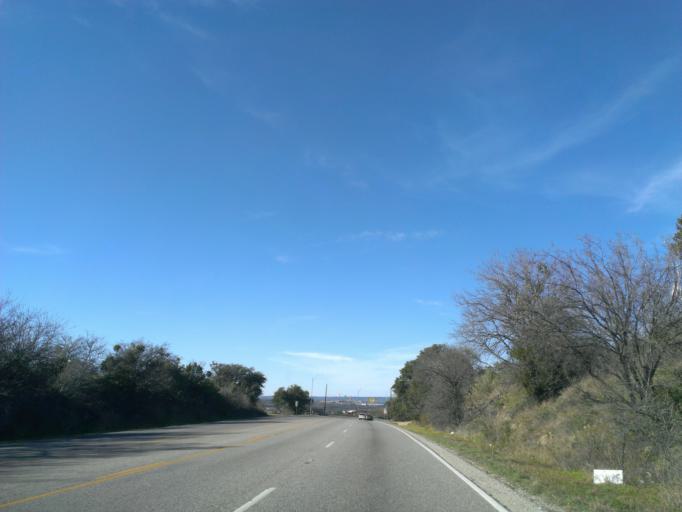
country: US
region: Texas
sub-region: Burnet County
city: Marble Falls
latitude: 30.5579
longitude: -98.2746
